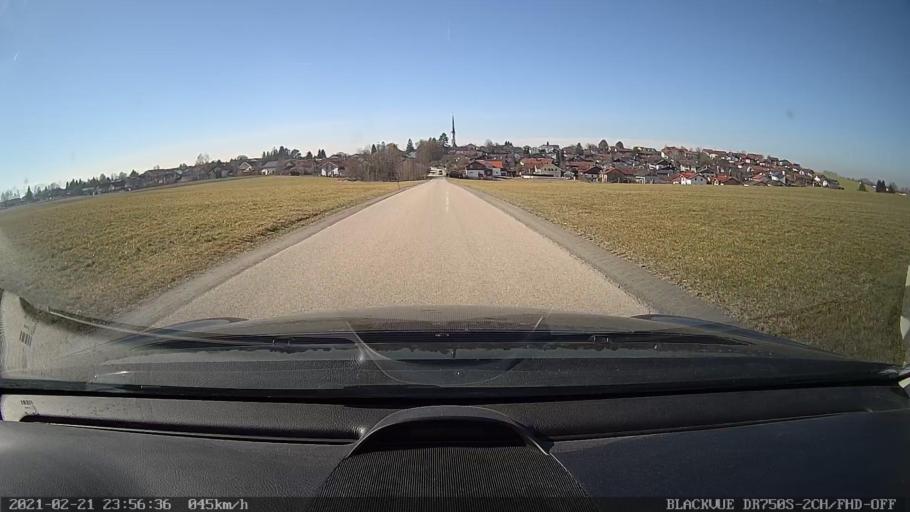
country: DE
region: Bavaria
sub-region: Upper Bavaria
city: Griesstatt
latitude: 47.9954
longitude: 12.1864
